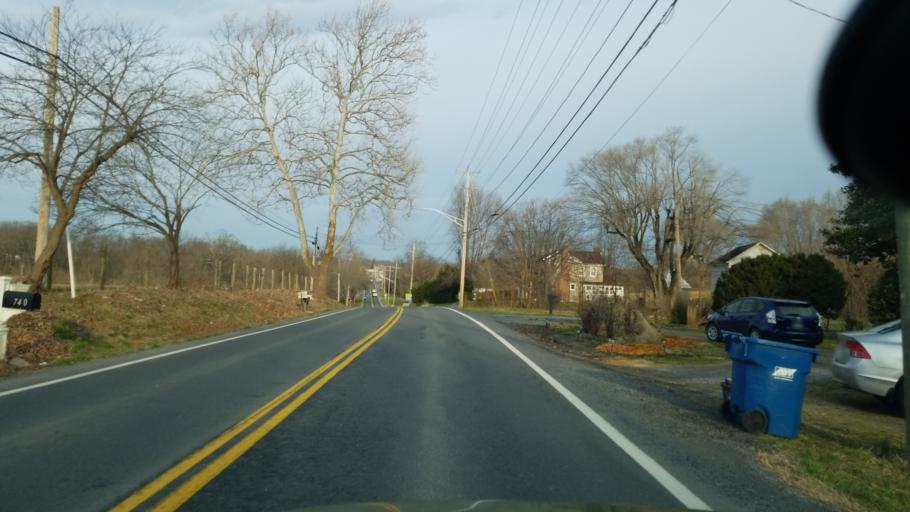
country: US
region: Virginia
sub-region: Clarke County
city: Berryville
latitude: 39.1458
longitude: -77.9646
